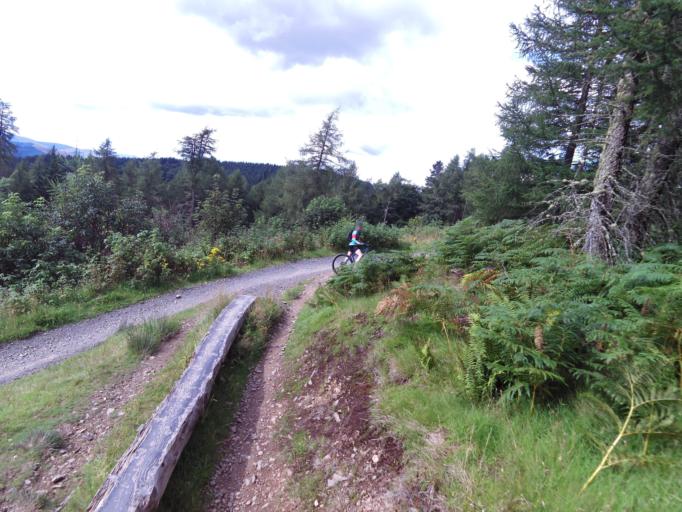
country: GB
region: Scotland
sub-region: The Scottish Borders
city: Peebles
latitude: 55.6567
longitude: -3.1498
